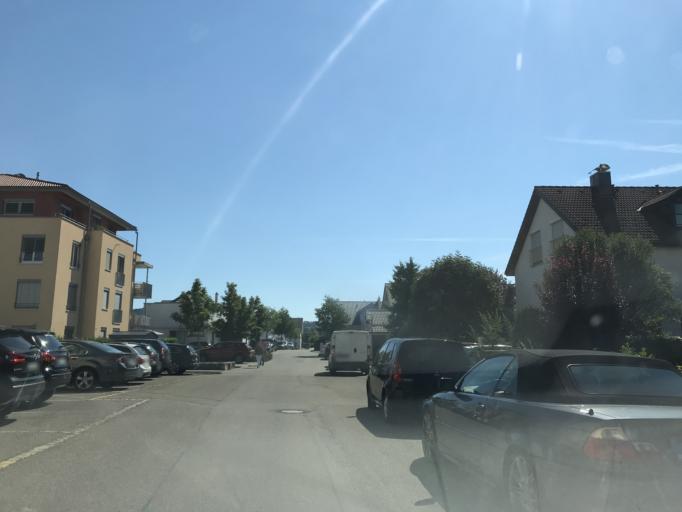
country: DE
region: Baden-Wuerttemberg
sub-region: Freiburg Region
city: Schopfheim
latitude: 47.6551
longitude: 7.8365
